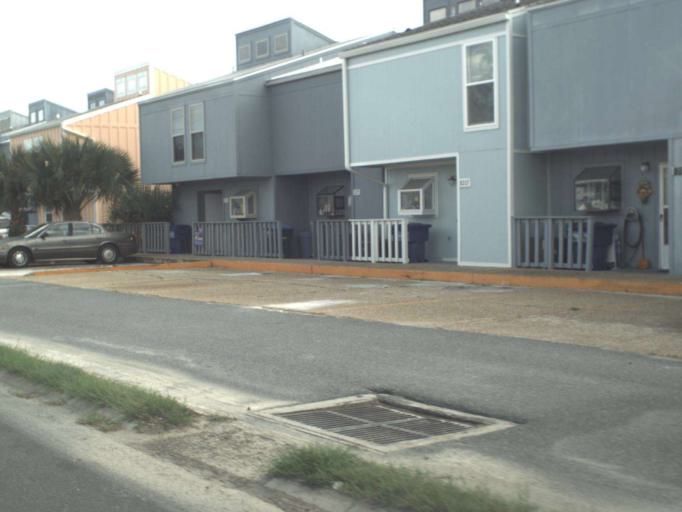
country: US
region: Florida
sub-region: Bay County
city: Mexico Beach
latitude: 29.9106
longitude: -85.3738
